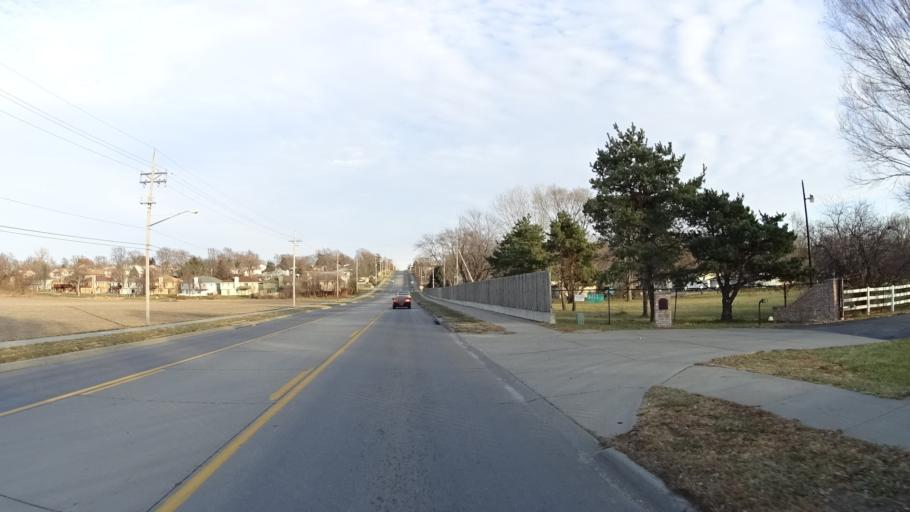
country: US
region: Nebraska
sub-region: Sarpy County
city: La Vista
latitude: 41.1907
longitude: -96.0024
